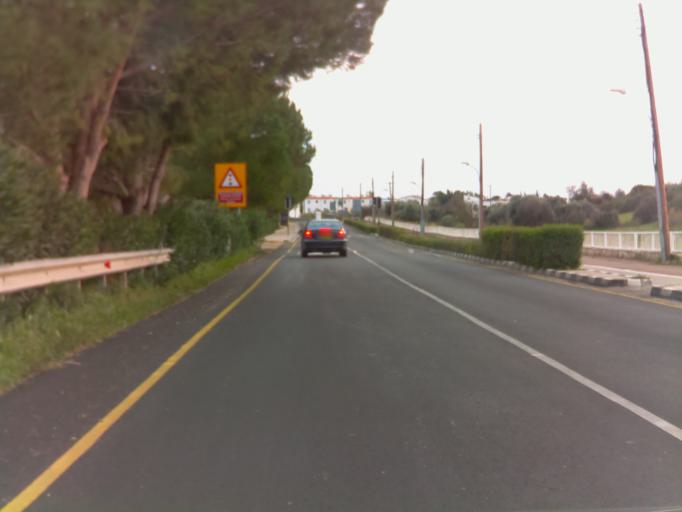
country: CY
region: Pafos
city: Polis
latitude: 35.0390
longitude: 32.4048
